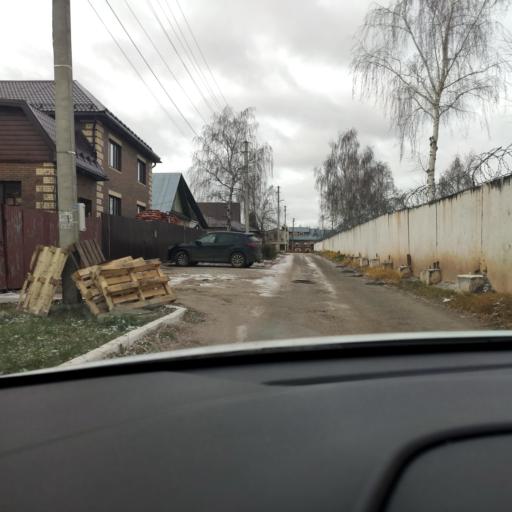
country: RU
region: Tatarstan
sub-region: Gorod Kazan'
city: Kazan
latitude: 55.8557
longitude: 49.0691
